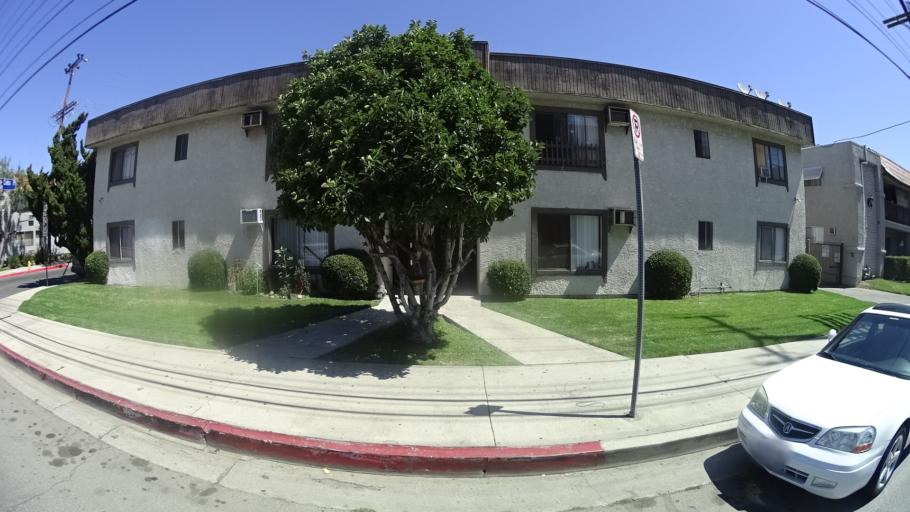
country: US
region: California
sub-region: Los Angeles County
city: Van Nuys
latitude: 34.1939
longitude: -118.4943
